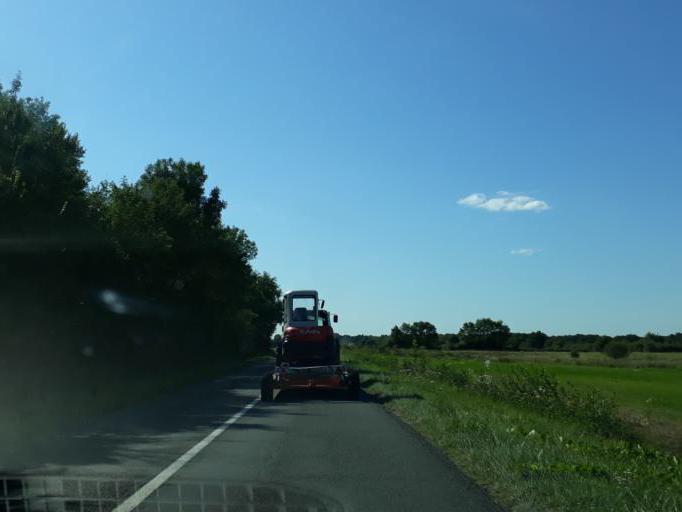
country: FR
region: Centre
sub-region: Departement du Loiret
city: Chateauneuf-sur-Loire
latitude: 47.8493
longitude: 2.2587
